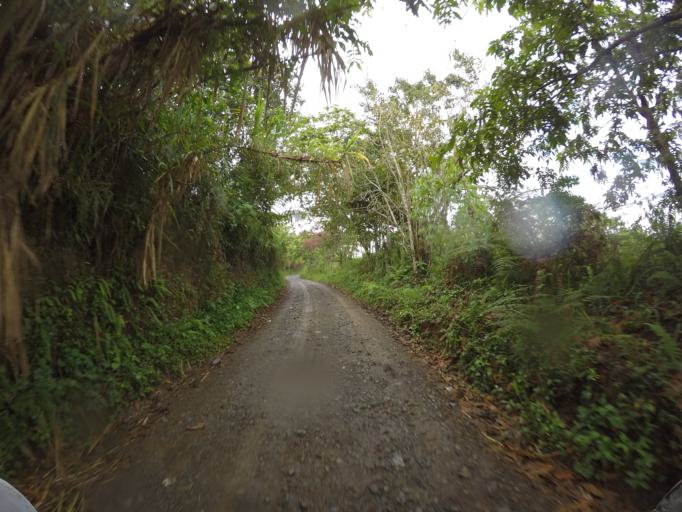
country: CO
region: Valle del Cauca
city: Ulloa
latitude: 4.6812
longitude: -75.7055
